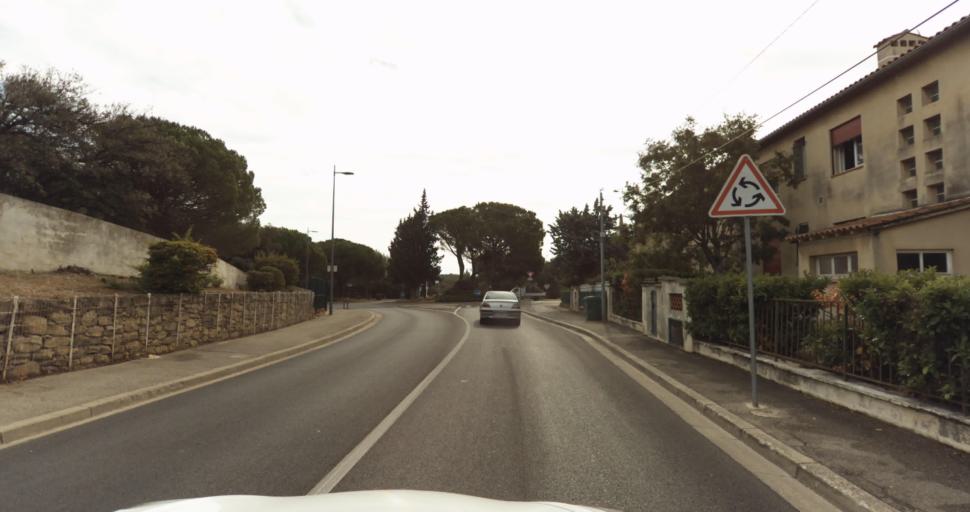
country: FR
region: Provence-Alpes-Cote d'Azur
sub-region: Departement des Bouches-du-Rhone
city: Miramas
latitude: 43.5910
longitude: 5.0085
